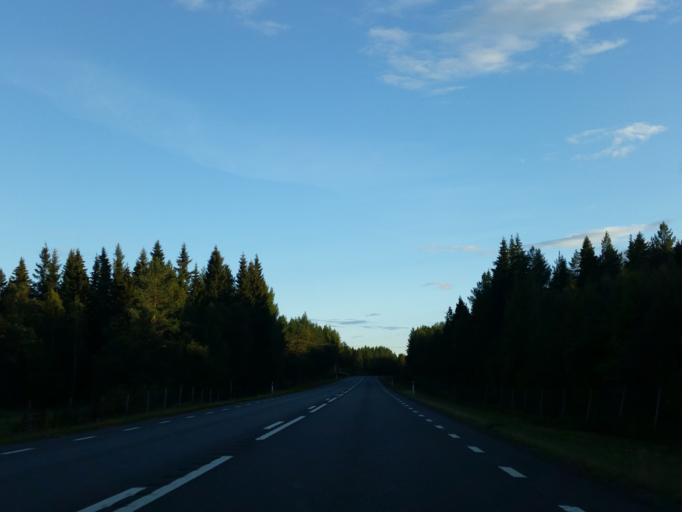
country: SE
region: Vaesterbotten
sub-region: Robertsfors Kommun
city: Robertsfors
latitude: 64.0282
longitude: 20.8414
